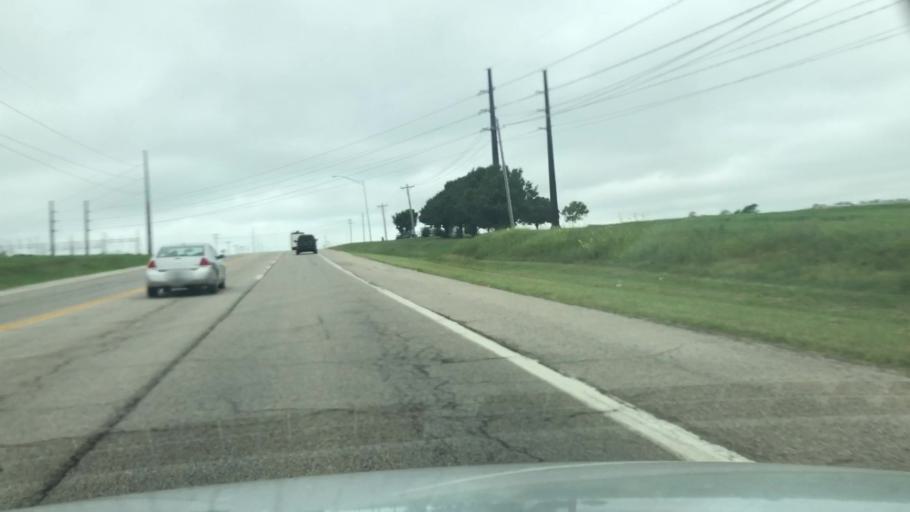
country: US
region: Oklahoma
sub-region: Washington County
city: Dewey
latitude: 36.7280
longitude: -95.8932
